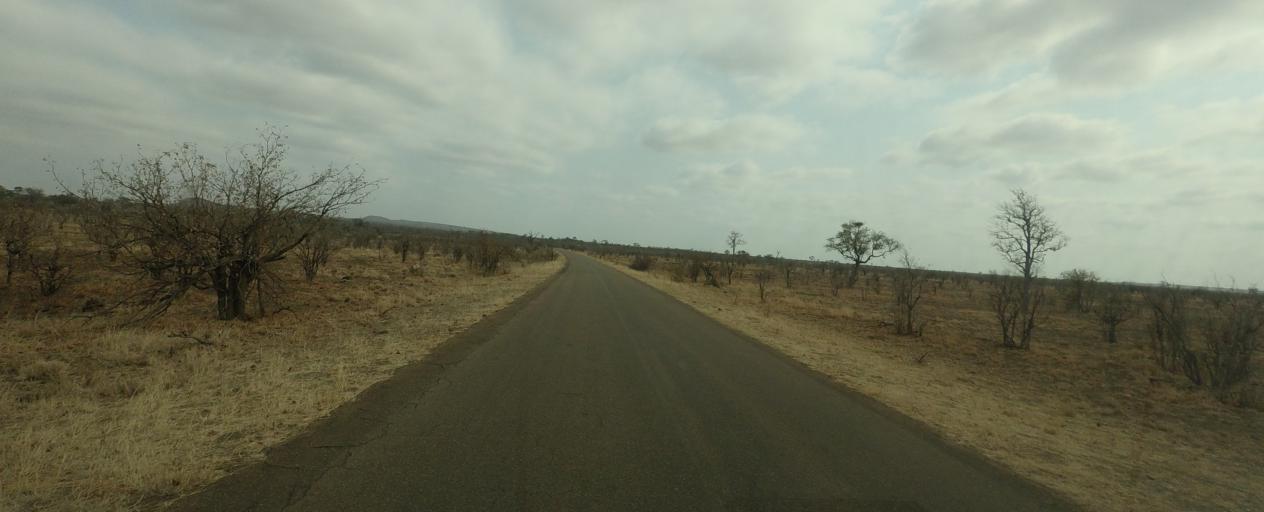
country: ZA
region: Limpopo
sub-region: Vhembe District Municipality
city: Mutale
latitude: -22.6293
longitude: 31.1796
